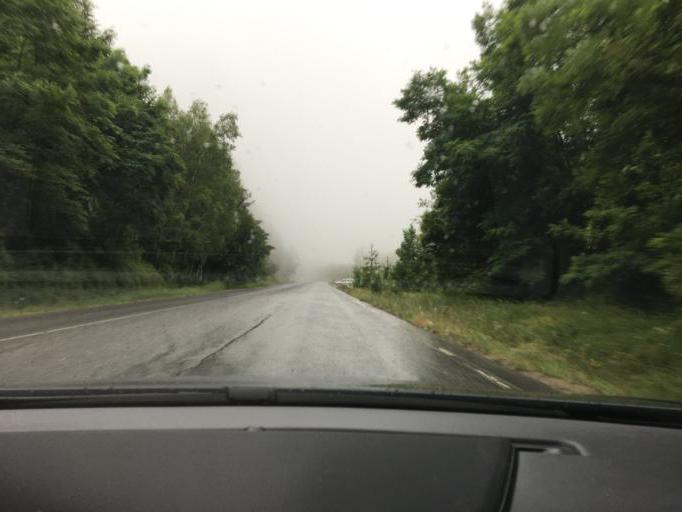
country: MK
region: Kriva Palanka
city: Kriva Palanka
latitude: 42.2173
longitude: 22.4690
